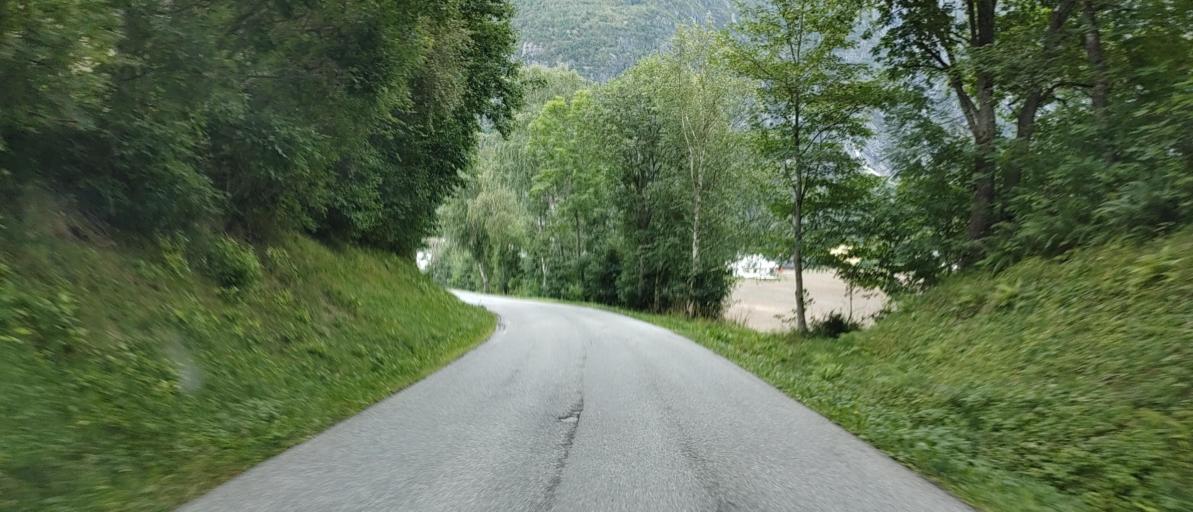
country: NO
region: More og Romsdal
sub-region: Rauma
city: Andalsnes
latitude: 62.5272
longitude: 7.7206
